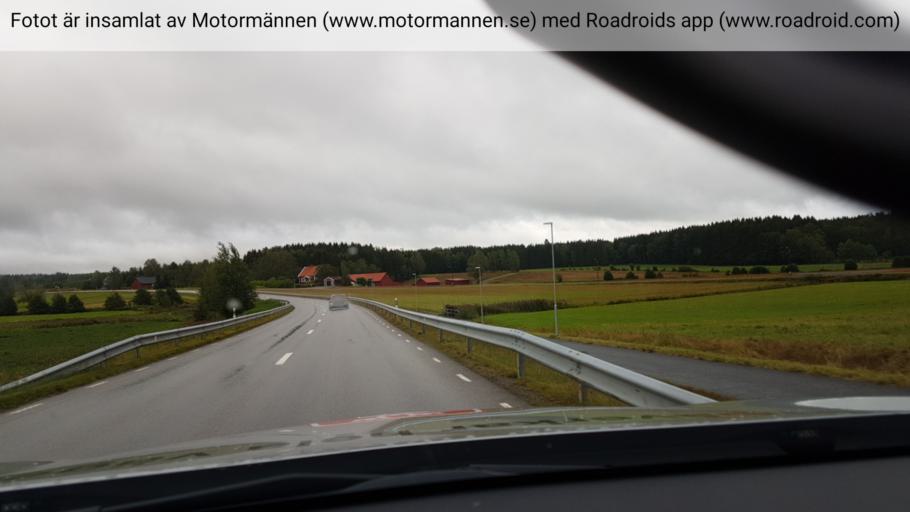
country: SE
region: Vaestra Goetaland
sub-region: Alingsas Kommun
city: Sollebrunn
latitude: 58.1085
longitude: 12.5851
